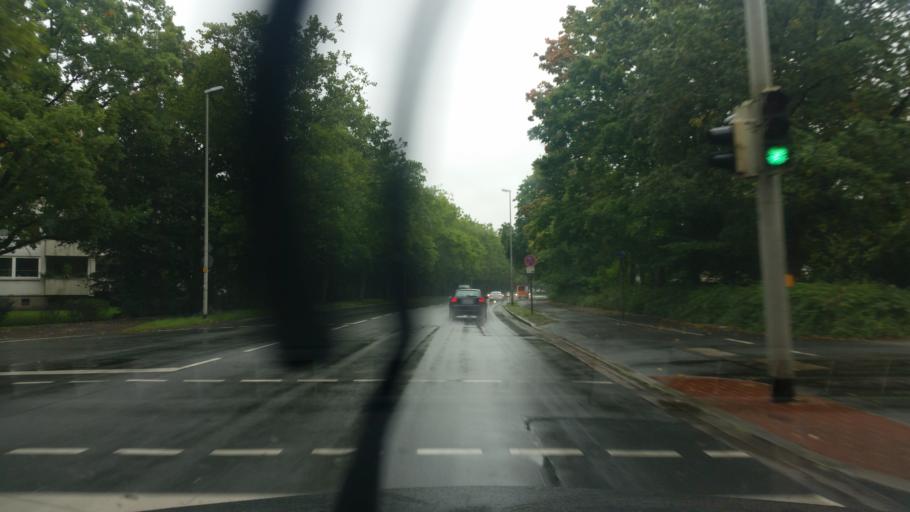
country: DE
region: Lower Saxony
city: Hannover
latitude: 52.3980
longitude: 9.7855
